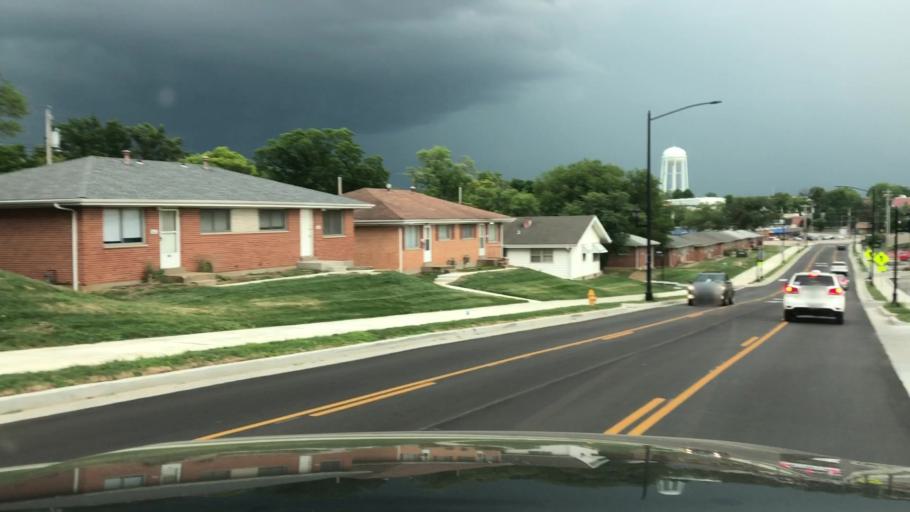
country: US
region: Missouri
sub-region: Saint Charles County
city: Saint Charles
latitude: 38.7869
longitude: -90.5115
